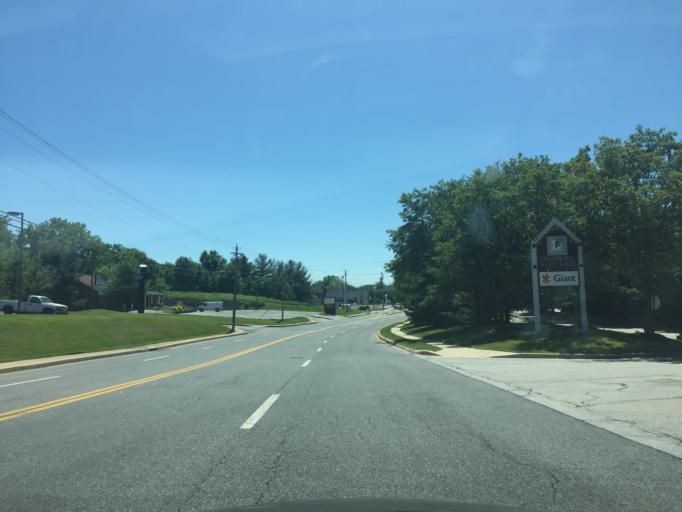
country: US
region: Maryland
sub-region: Carroll County
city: Westminster
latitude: 39.5735
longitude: -76.9812
